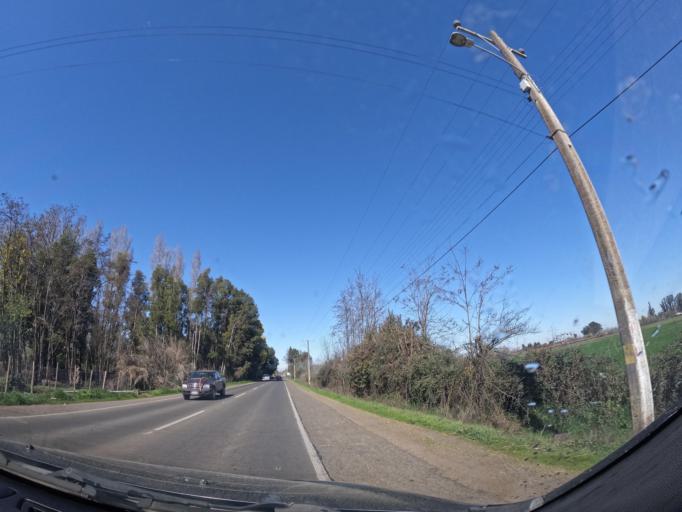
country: CL
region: Maule
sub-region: Provincia de Linares
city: Parral
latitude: -36.1510
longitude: -71.7501
